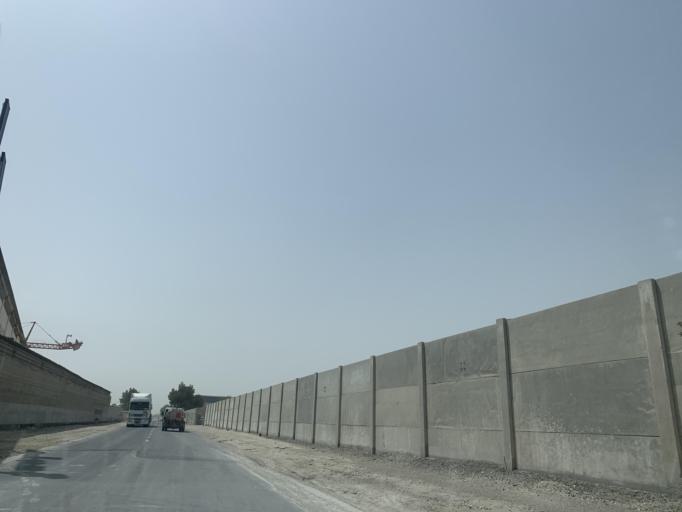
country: BH
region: Northern
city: Madinat `Isa
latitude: 26.1915
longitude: 50.5344
